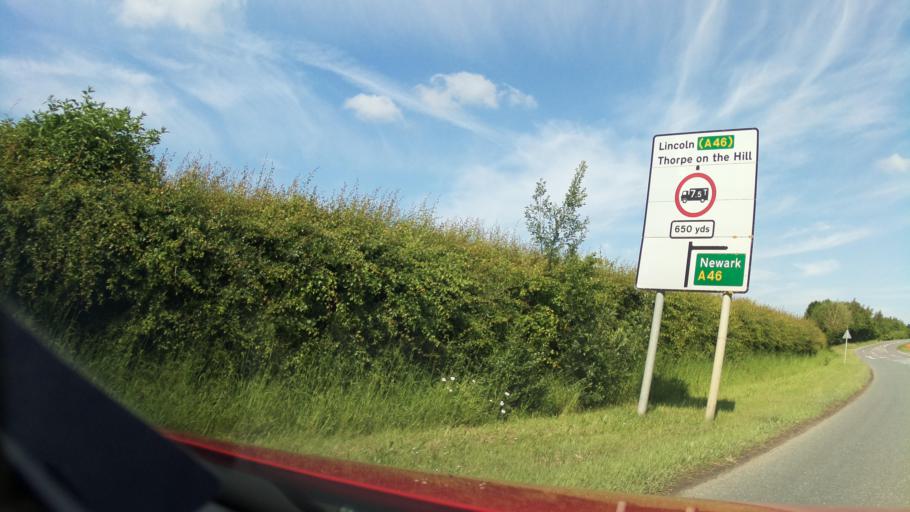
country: GB
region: England
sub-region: Lincolnshire
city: Skellingthorpe
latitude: 53.1657
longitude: -0.6401
